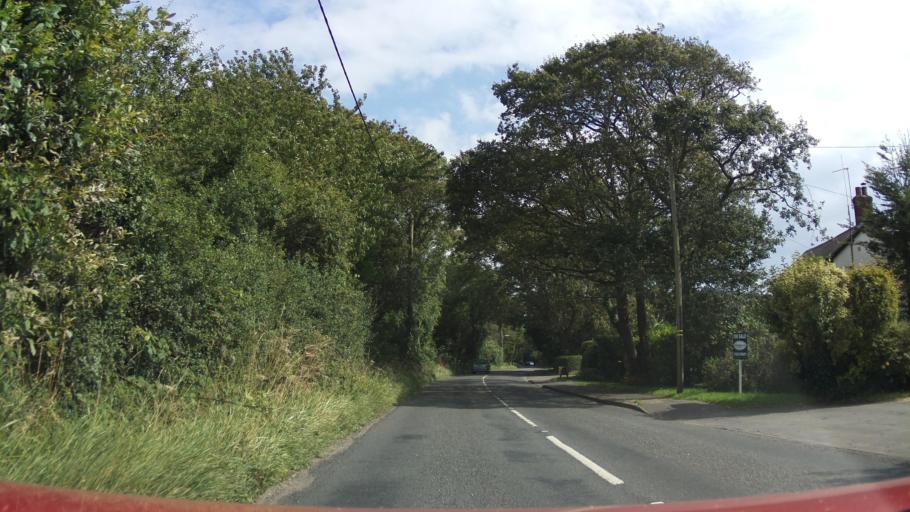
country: GB
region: England
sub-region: Hampshire
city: New Milton
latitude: 50.7438
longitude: -1.6481
